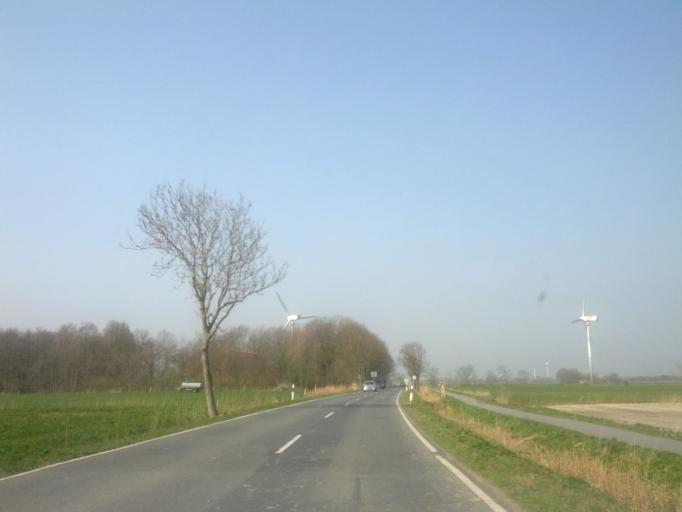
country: DE
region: Lower Saxony
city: Dornum
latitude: 53.6696
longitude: 7.4236
